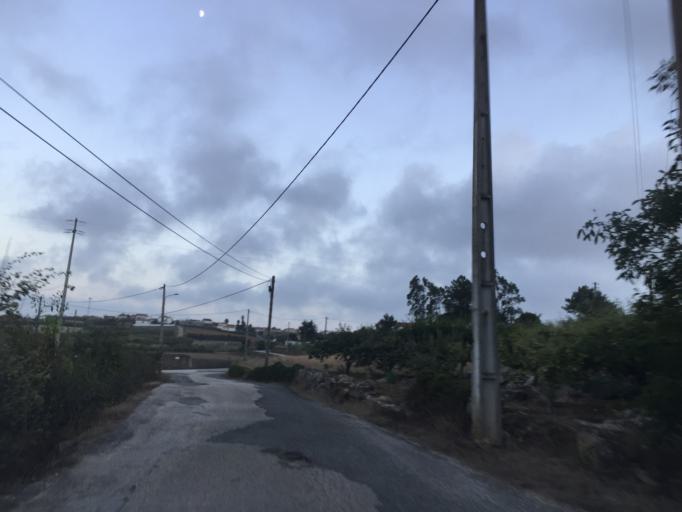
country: PT
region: Leiria
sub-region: Bombarral
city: Bombarral
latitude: 39.2866
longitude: -9.2247
